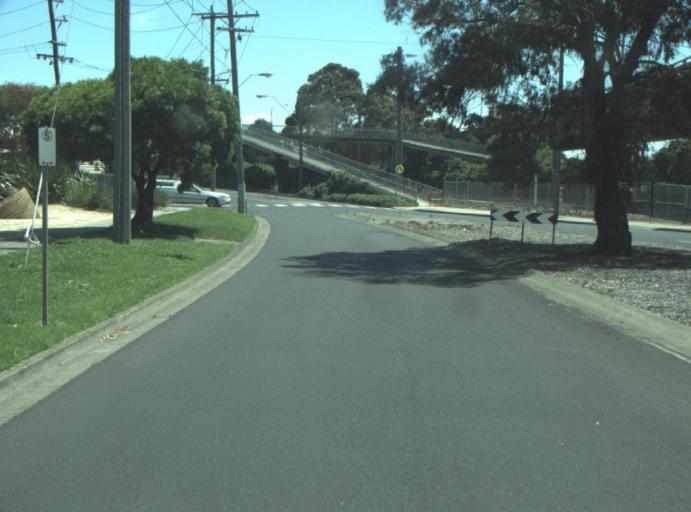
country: AU
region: Victoria
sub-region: Greater Geelong
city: Geelong West
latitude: -38.1401
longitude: 144.3536
